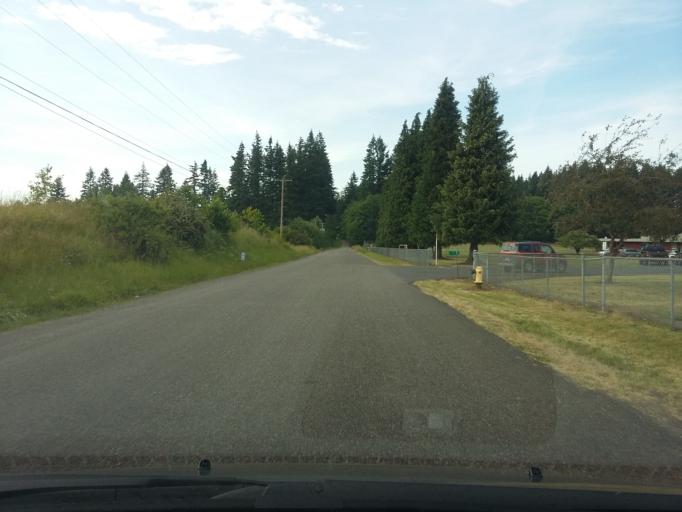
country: US
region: Washington
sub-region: Clark County
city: Brush Prairie
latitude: 45.7199
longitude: -122.5732
